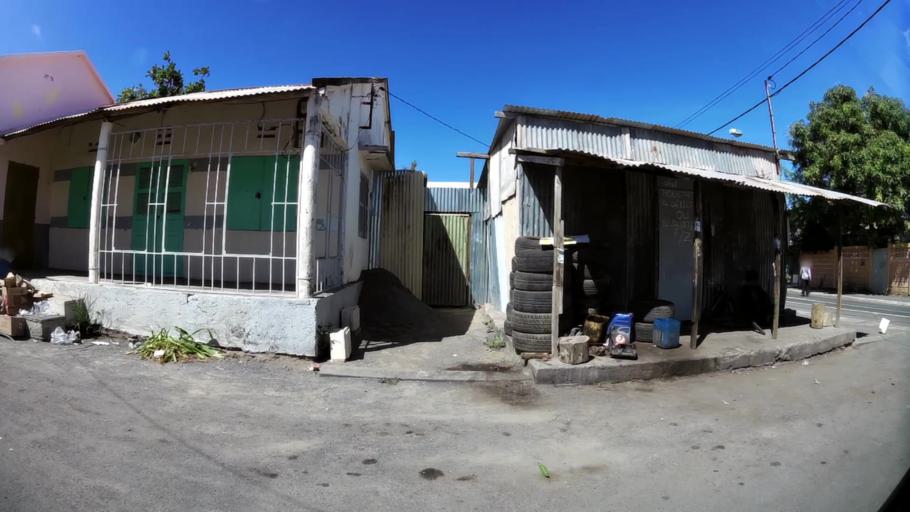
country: YT
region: Pamandzi
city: Pamandzi
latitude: -12.8003
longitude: 45.2784
